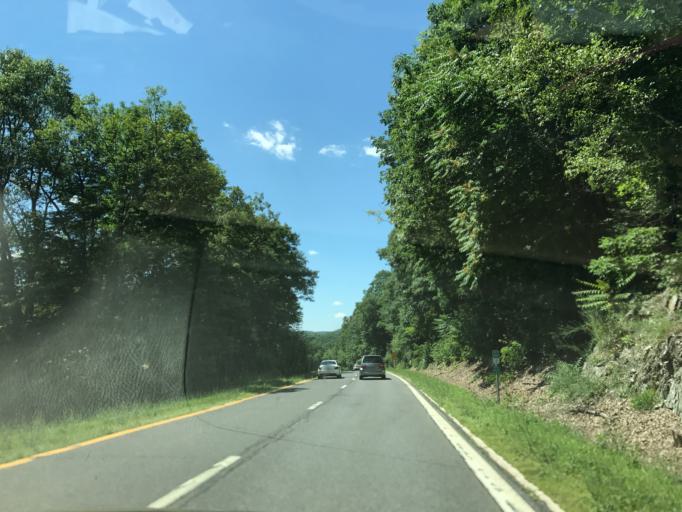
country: US
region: New York
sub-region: Dutchess County
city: Pleasant Valley
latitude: 41.7806
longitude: -73.7693
